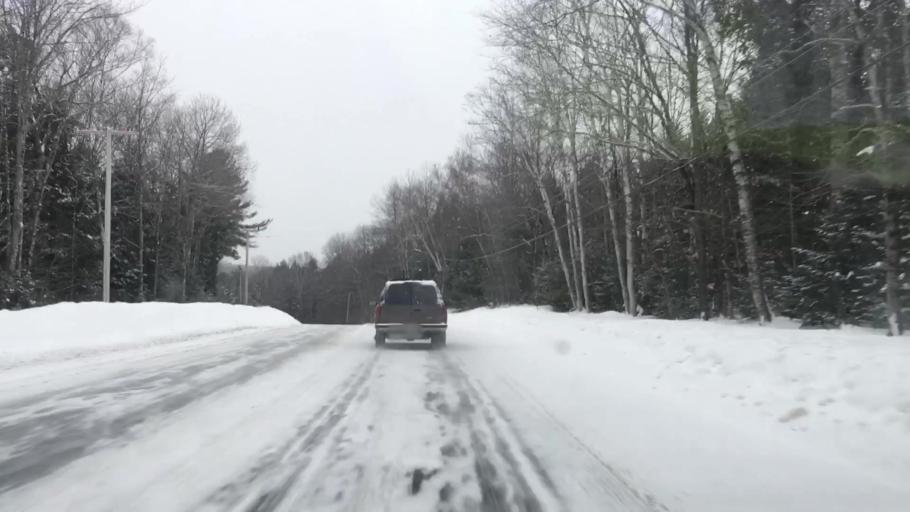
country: US
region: Maine
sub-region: Penobscot County
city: Medway
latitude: 45.5995
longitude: -68.4617
